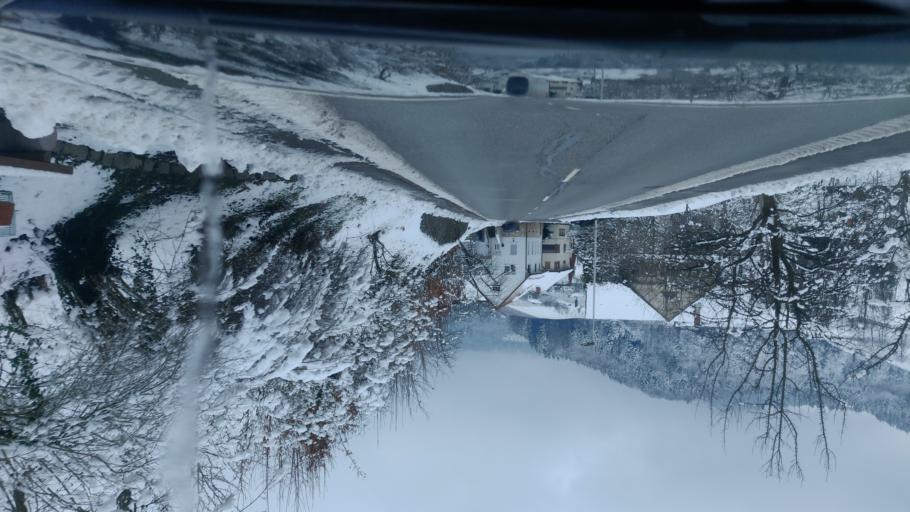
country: DE
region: Baden-Wuerttemberg
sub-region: Freiburg Region
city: Kappelrodeck
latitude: 48.5833
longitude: 8.1033
